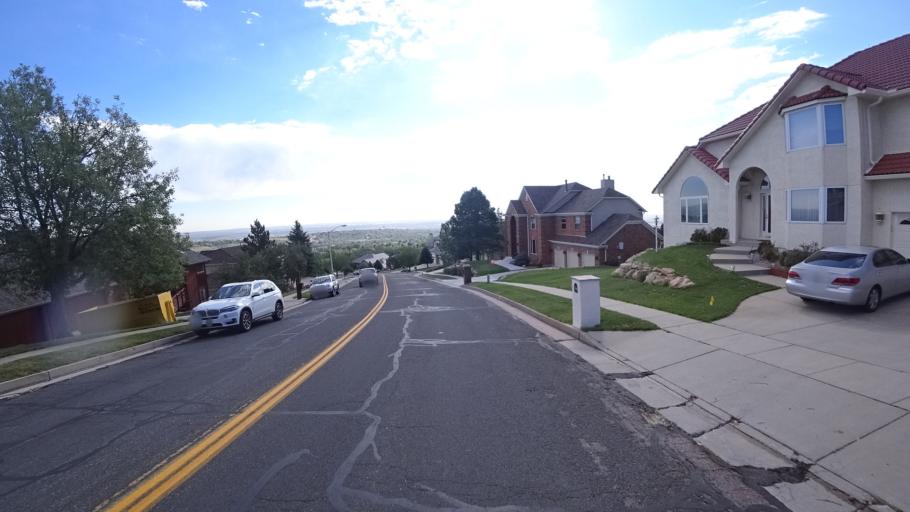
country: US
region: Colorado
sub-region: El Paso County
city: Stratmoor
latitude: 38.7705
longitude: -104.8256
